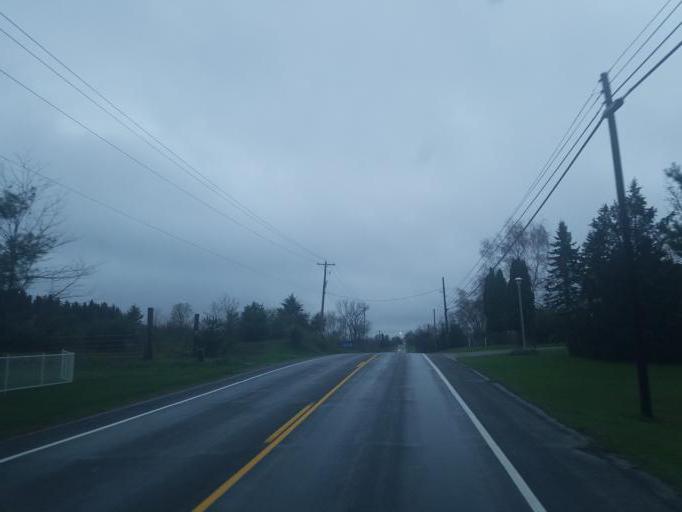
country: US
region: Michigan
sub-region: Montcalm County
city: Edmore
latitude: 43.4120
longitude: -85.0441
